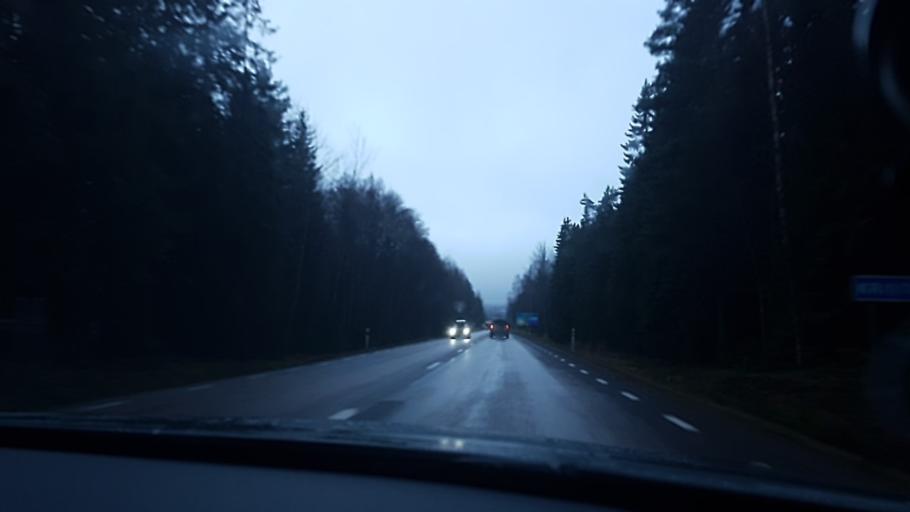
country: SE
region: Vaermland
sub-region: Kristinehamns Kommun
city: Kristinehamn
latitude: 59.3305
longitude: 14.1184
